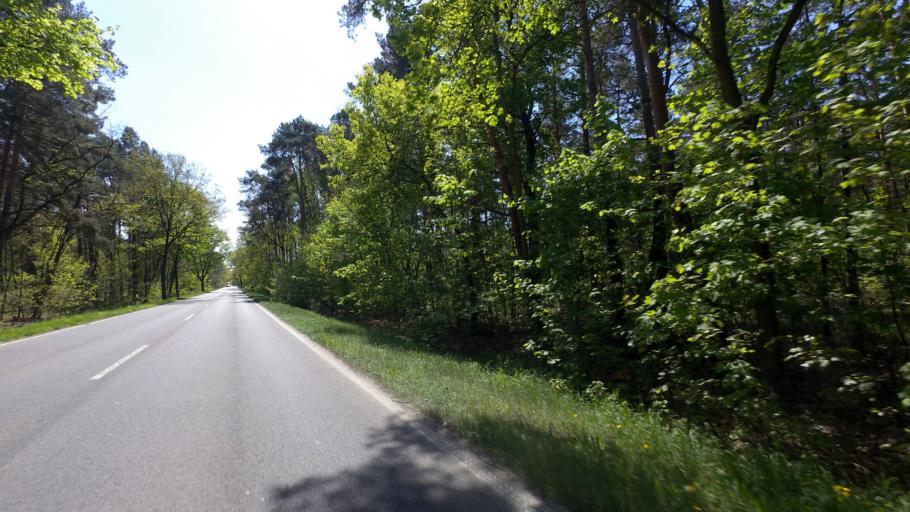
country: DE
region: Brandenburg
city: Bestensee
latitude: 52.2521
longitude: 13.6563
